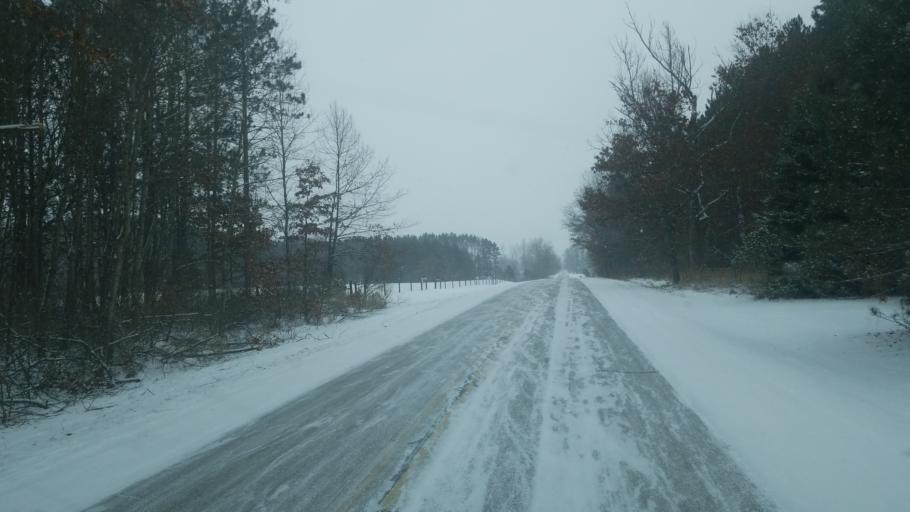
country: US
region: Michigan
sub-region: Mecosta County
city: Big Rapids
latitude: 43.7425
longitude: -85.4033
